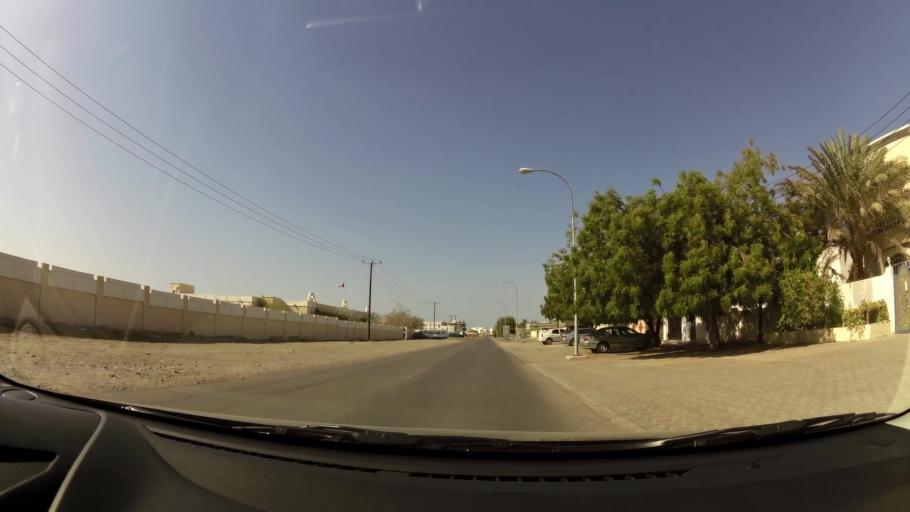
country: OM
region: Muhafazat Masqat
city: As Sib al Jadidah
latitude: 23.6312
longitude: 58.2014
